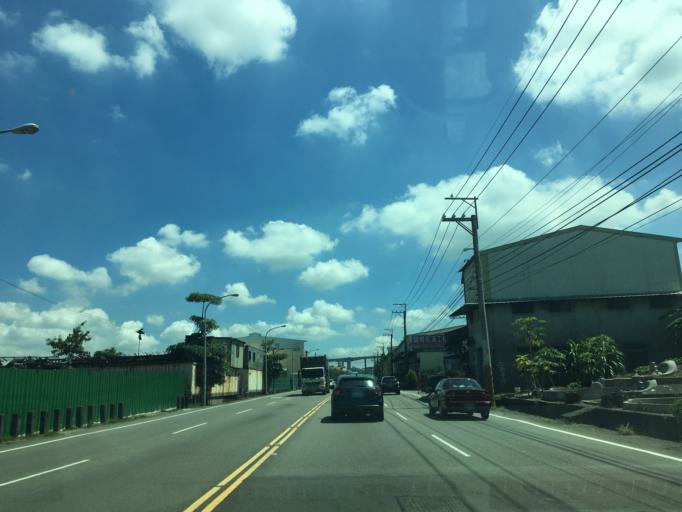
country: TW
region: Taiwan
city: Fengyuan
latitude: 24.2104
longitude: 120.7220
